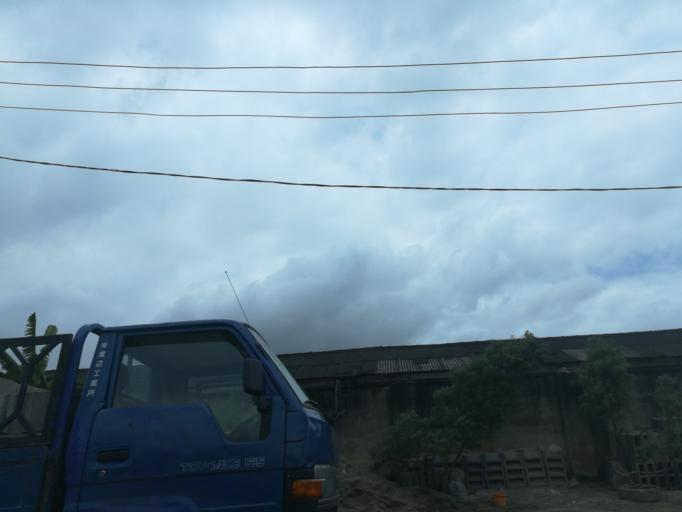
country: NG
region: Lagos
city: Lagos
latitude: 6.4528
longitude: 3.4025
